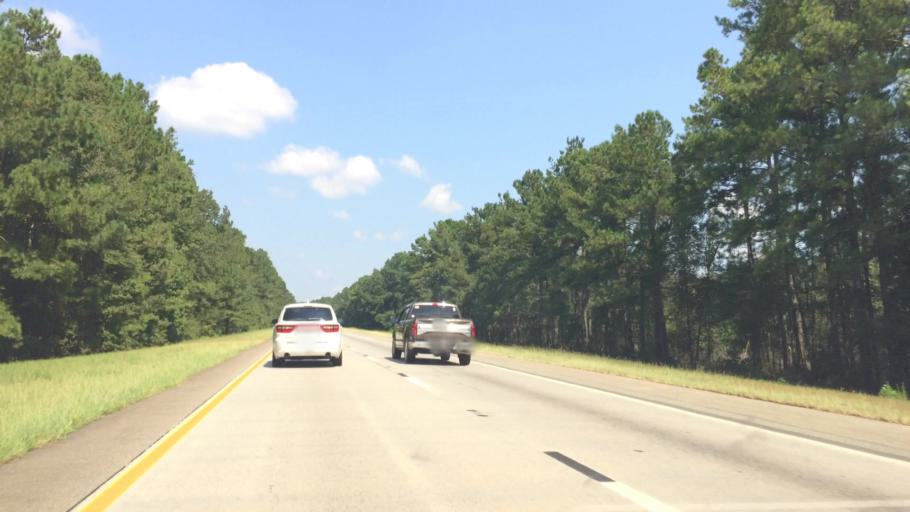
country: US
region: South Carolina
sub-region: Colleton County
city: Walterboro
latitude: 33.0109
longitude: -80.6672
